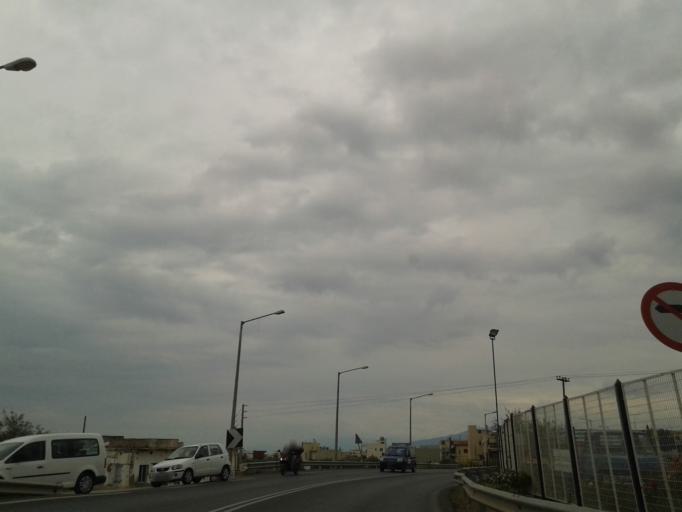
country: GR
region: Peloponnese
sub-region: Nomos Argolidos
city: Argos
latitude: 37.6478
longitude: 22.7296
